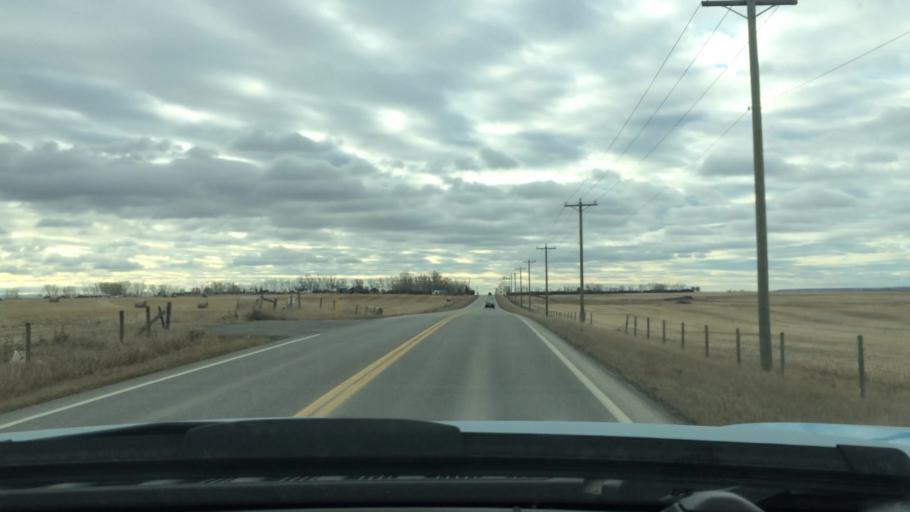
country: CA
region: Alberta
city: Airdrie
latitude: 51.2382
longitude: -114.0250
